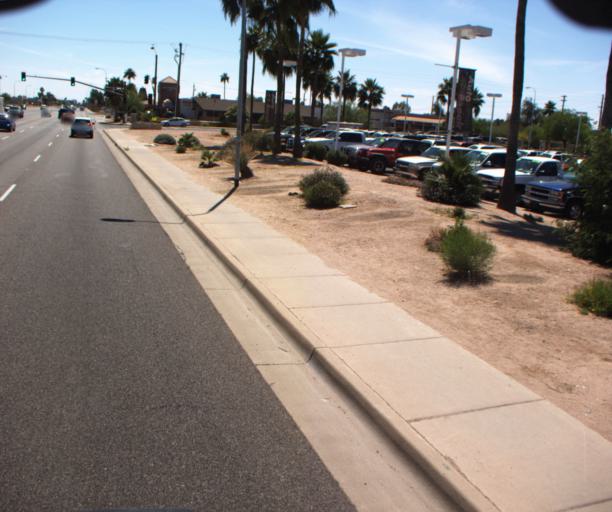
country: US
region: Arizona
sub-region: Maricopa County
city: San Carlos
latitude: 33.3287
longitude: -111.8418
